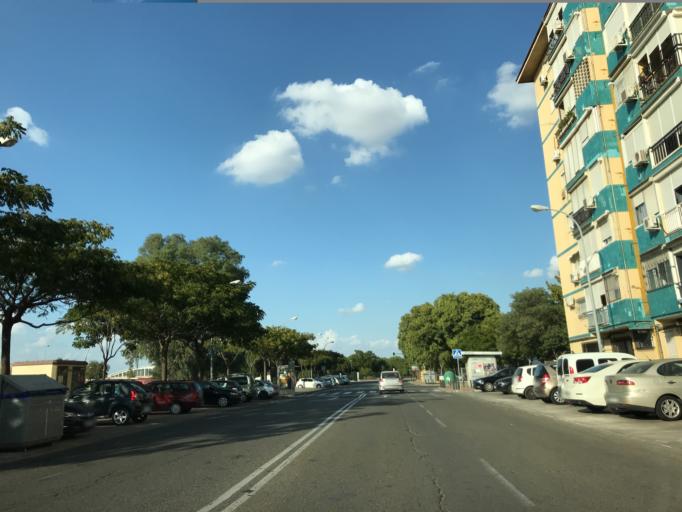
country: ES
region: Andalusia
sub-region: Provincia de Sevilla
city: Sevilla
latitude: 37.4118
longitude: -5.9257
